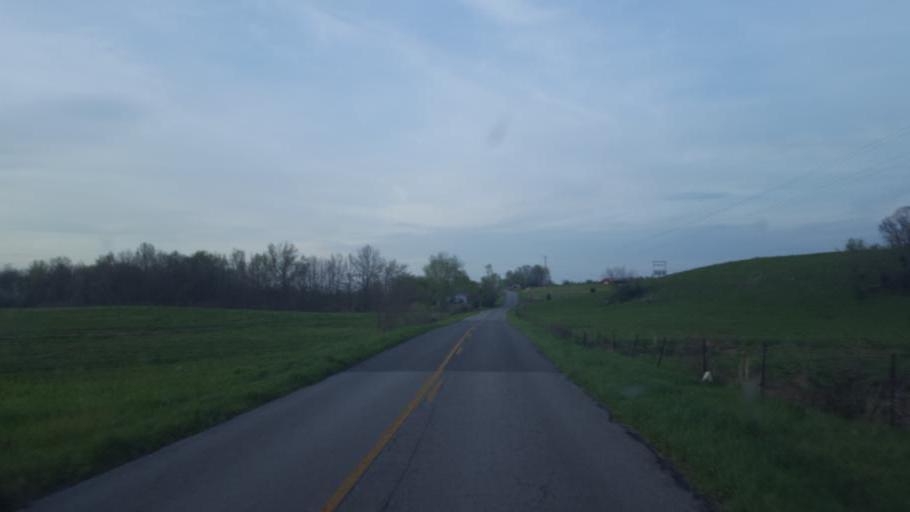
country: US
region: Kentucky
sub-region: Metcalfe County
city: Edmonton
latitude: 37.1296
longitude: -85.6953
